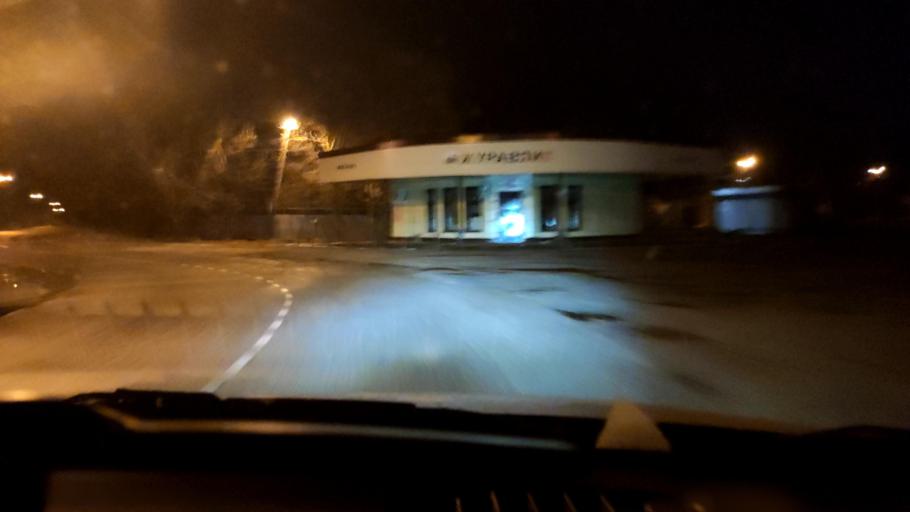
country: RU
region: Voronezj
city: Somovo
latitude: 51.7391
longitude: 39.3469
